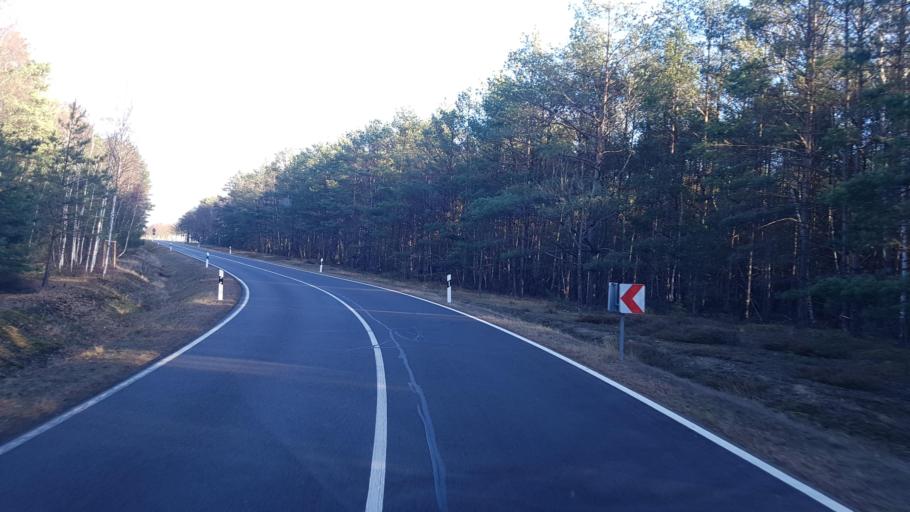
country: DE
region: Brandenburg
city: Forst
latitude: 51.7492
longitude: 14.5602
